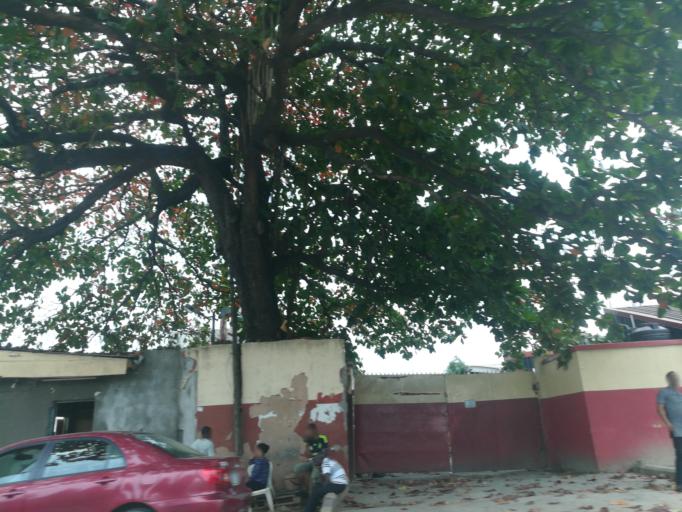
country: NG
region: Lagos
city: Ikeja
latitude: 6.6068
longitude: 3.3609
